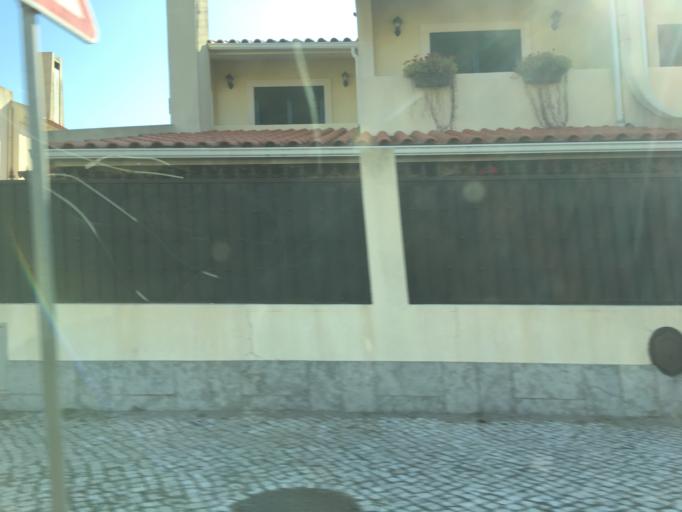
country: PT
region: Lisbon
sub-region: Cascais
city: Parede
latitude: 38.7197
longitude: -9.3484
